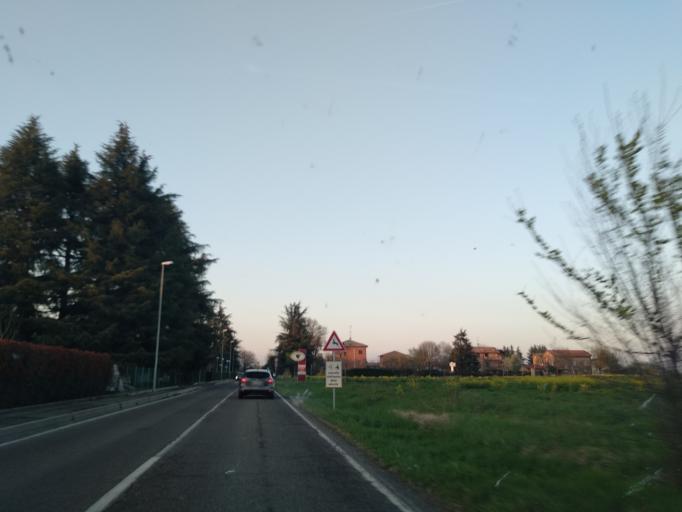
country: IT
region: Emilia-Romagna
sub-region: Provincia di Reggio Emilia
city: Forche
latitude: 44.6502
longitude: 10.5862
